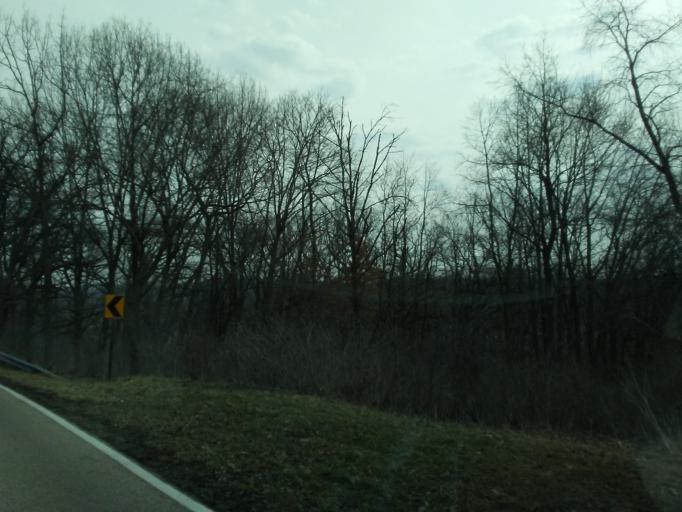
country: US
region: Wisconsin
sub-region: Dane County
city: Middleton
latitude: 43.1112
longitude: -89.4919
